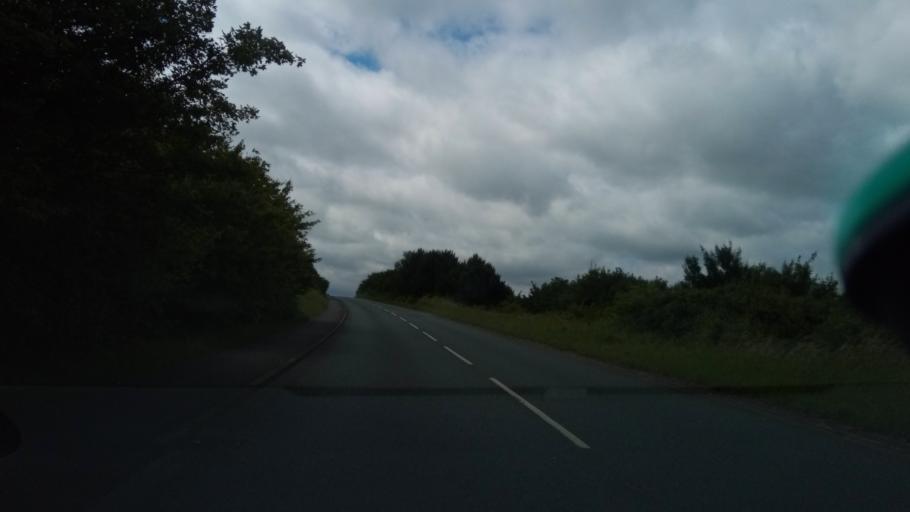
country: GB
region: England
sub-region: Derbyshire
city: Findern
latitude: 52.8723
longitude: -1.5100
